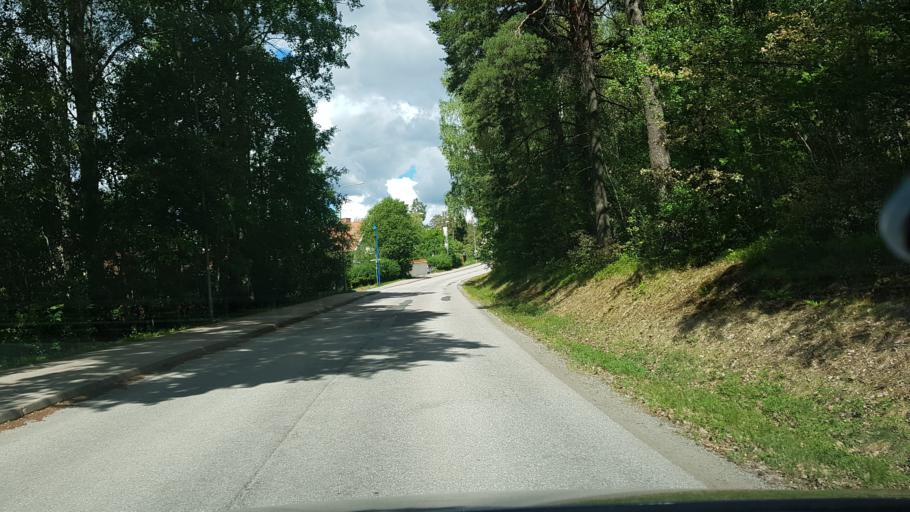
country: SE
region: Stockholm
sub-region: Upplands-Bro Kommun
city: Kungsaengen
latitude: 59.4770
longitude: 17.8068
